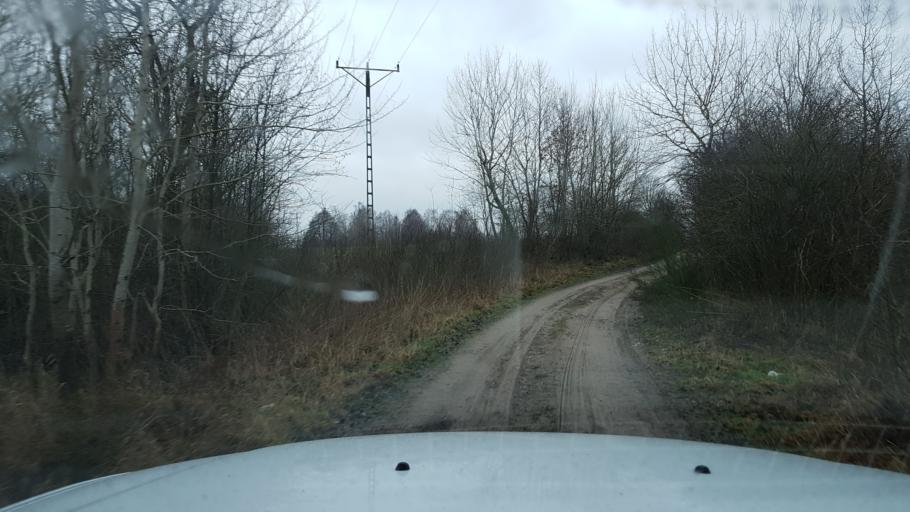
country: PL
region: West Pomeranian Voivodeship
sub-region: Powiat gryficki
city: Brojce
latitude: 53.9774
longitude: 15.3047
